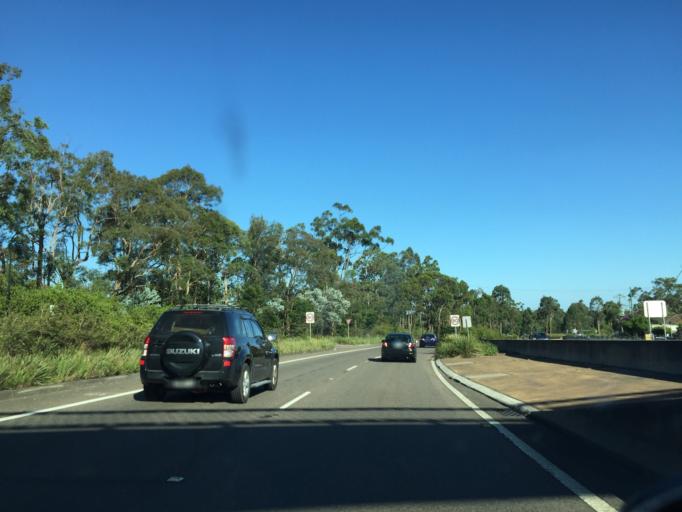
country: AU
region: New South Wales
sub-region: Blue Mountains Municipality
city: Blaxland
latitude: -33.7218
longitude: 150.6027
